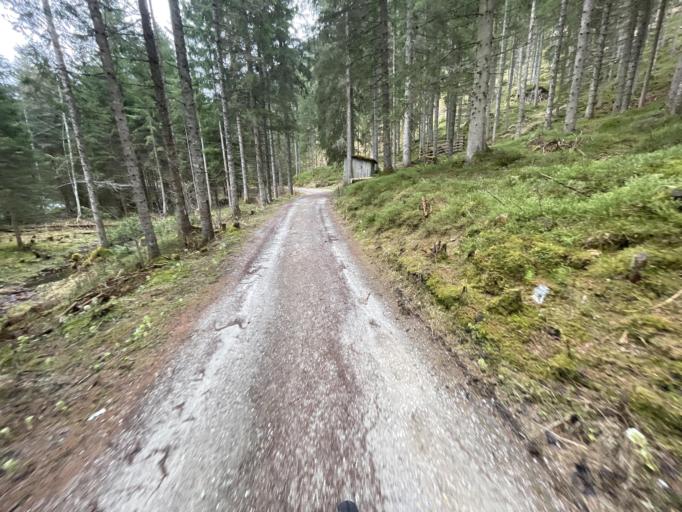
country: AT
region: Styria
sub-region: Politischer Bezirk Liezen
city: Schladming
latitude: 47.3556
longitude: 13.7021
